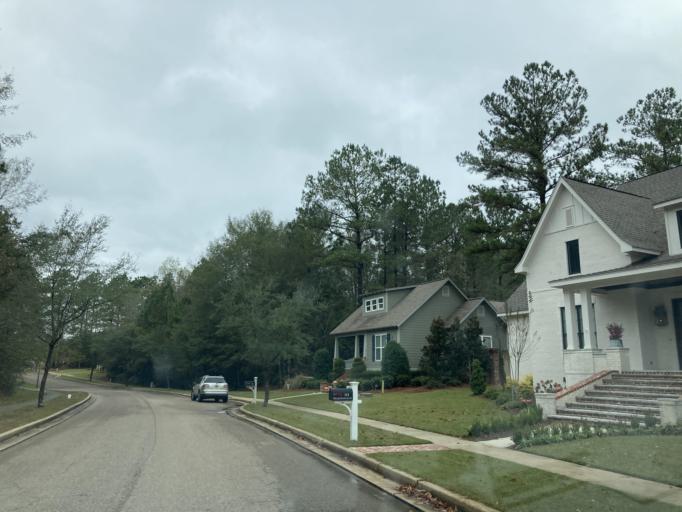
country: US
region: Mississippi
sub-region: Lamar County
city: West Hattiesburg
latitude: 31.2858
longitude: -89.4790
